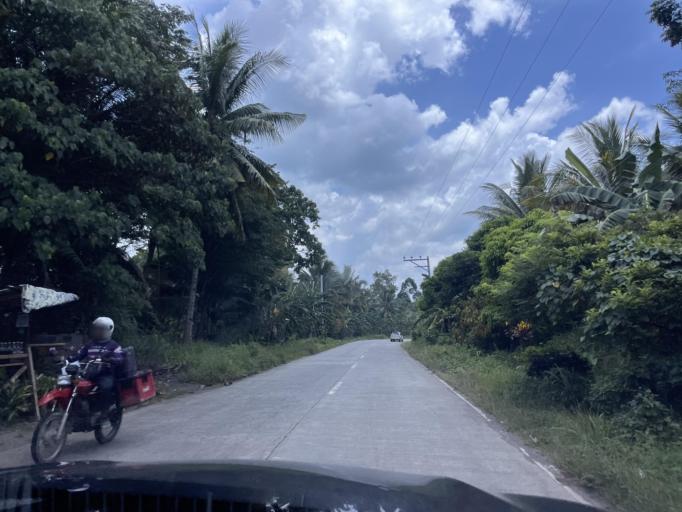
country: PH
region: Davao
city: Lacson
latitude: 7.2281
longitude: 125.4480
